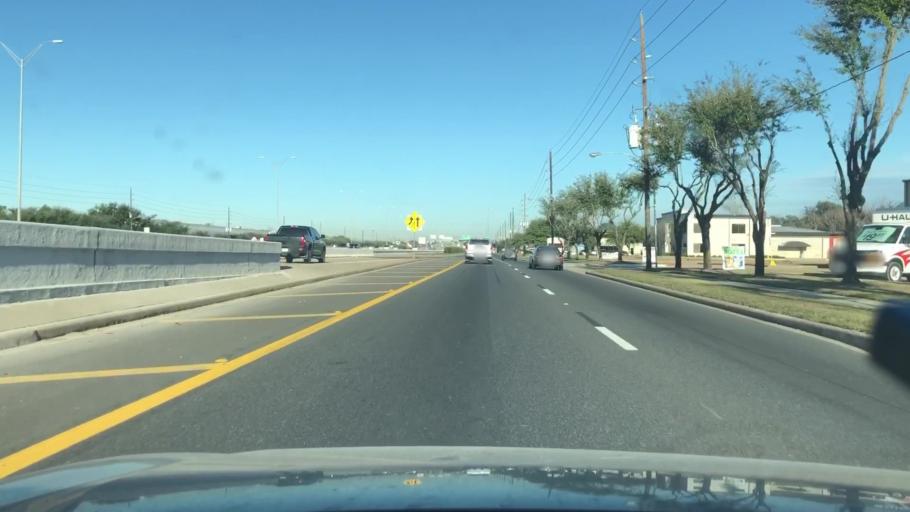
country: US
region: Texas
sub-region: Fort Bend County
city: Missouri City
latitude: 29.6473
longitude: -95.5423
